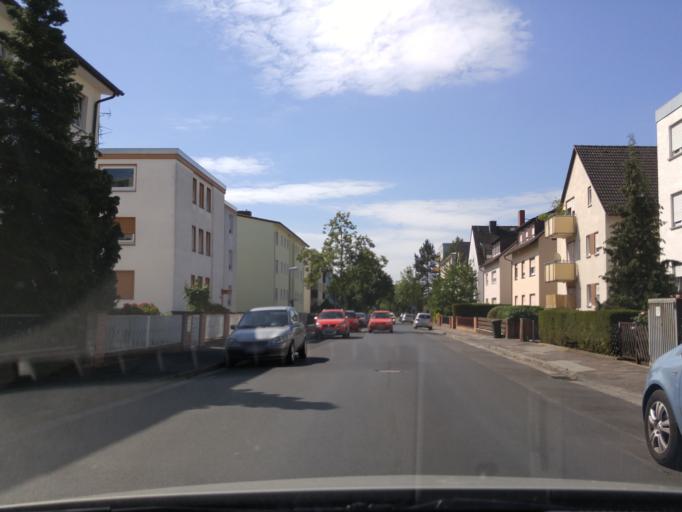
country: DE
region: Hesse
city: Dreieich
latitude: 50.0258
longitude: 8.6874
